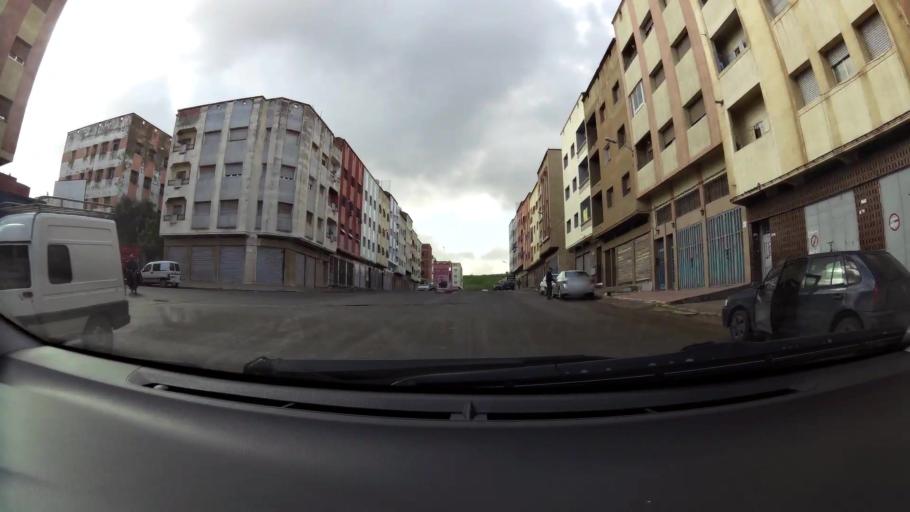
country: MA
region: Grand Casablanca
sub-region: Mediouna
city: Tit Mellil
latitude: 33.5784
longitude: -7.5353
